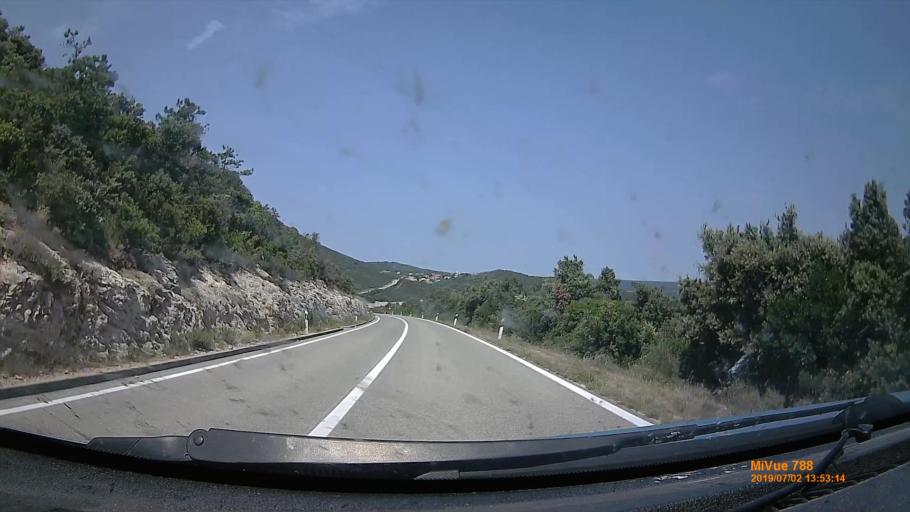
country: HR
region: Primorsko-Goranska
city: Mali Losinj
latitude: 44.6236
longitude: 14.3938
